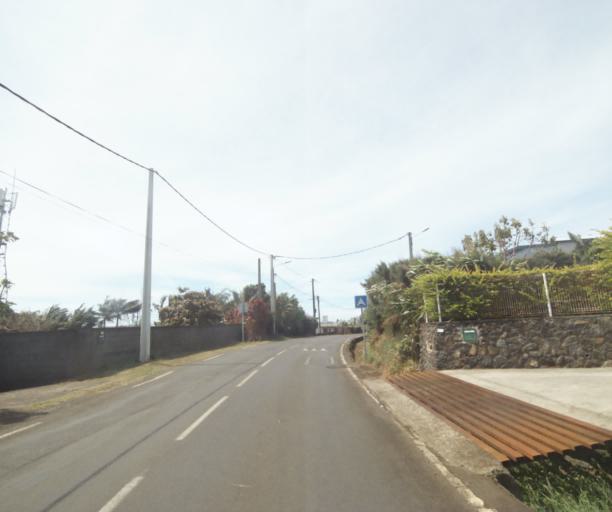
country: RE
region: Reunion
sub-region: Reunion
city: Saint-Paul
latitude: -21.0520
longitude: 55.2804
